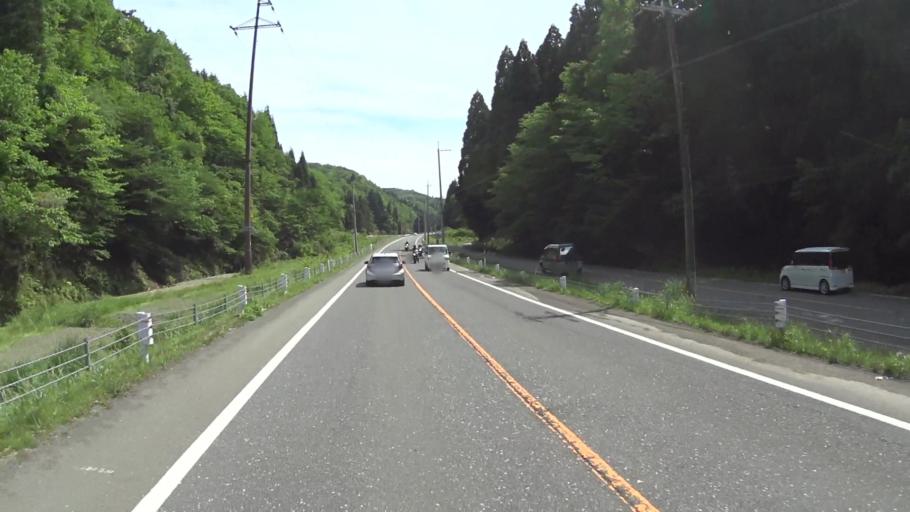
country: JP
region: Fukui
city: Obama
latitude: 35.4035
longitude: 135.9338
